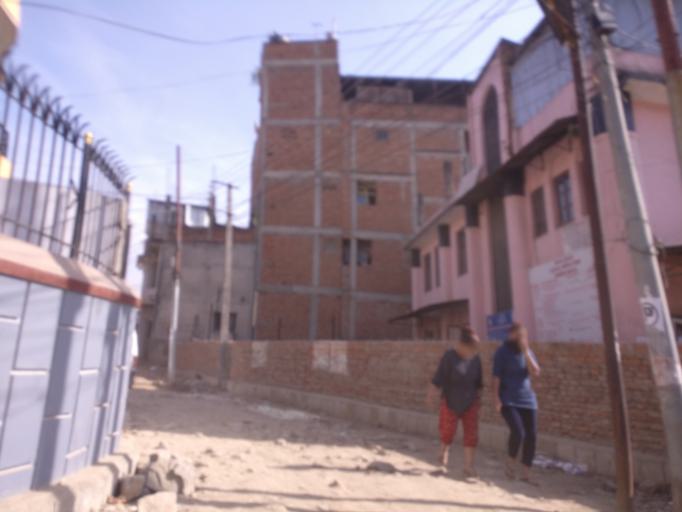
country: NP
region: Central Region
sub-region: Bagmati Zone
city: Patan
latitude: 27.6695
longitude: 85.3348
